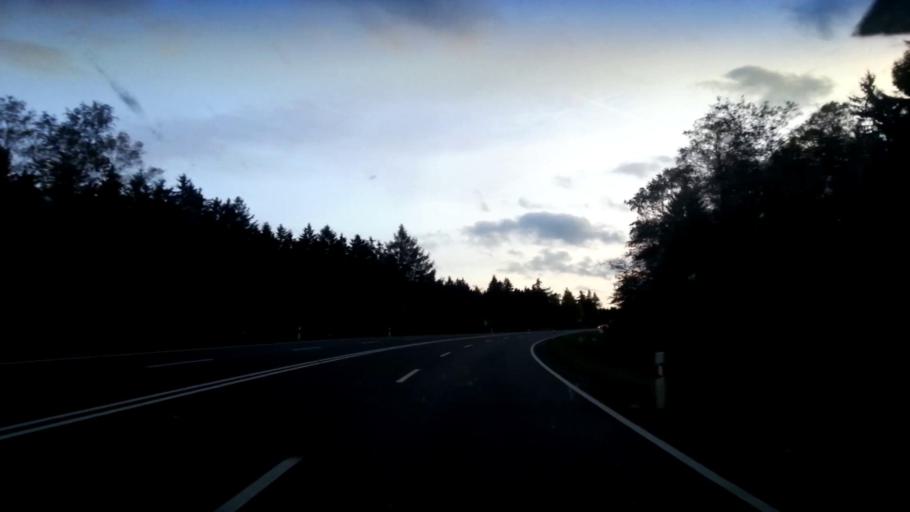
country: DE
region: Bavaria
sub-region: Upper Franconia
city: Trostau
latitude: 50.0084
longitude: 11.9251
